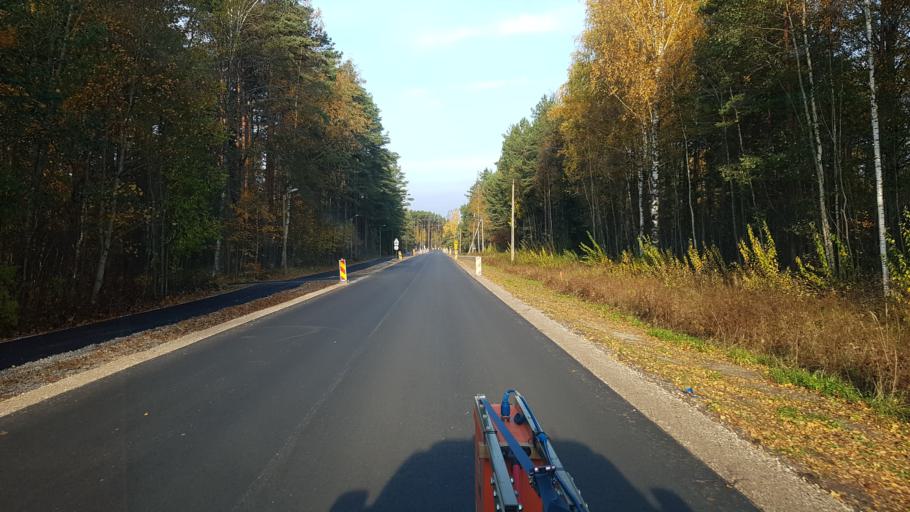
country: EE
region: Paernumaa
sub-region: Paikuse vald
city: Paikuse
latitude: 58.3589
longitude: 24.6116
